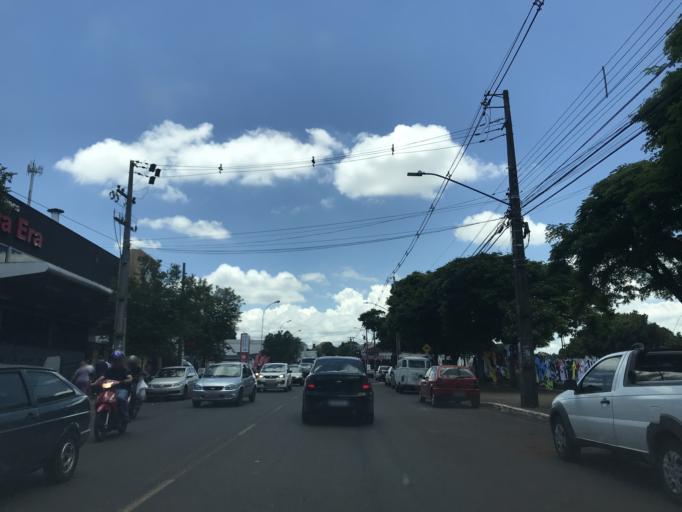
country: BR
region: Parana
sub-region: Marialva
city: Marialva
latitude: -23.4820
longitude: -51.8016
